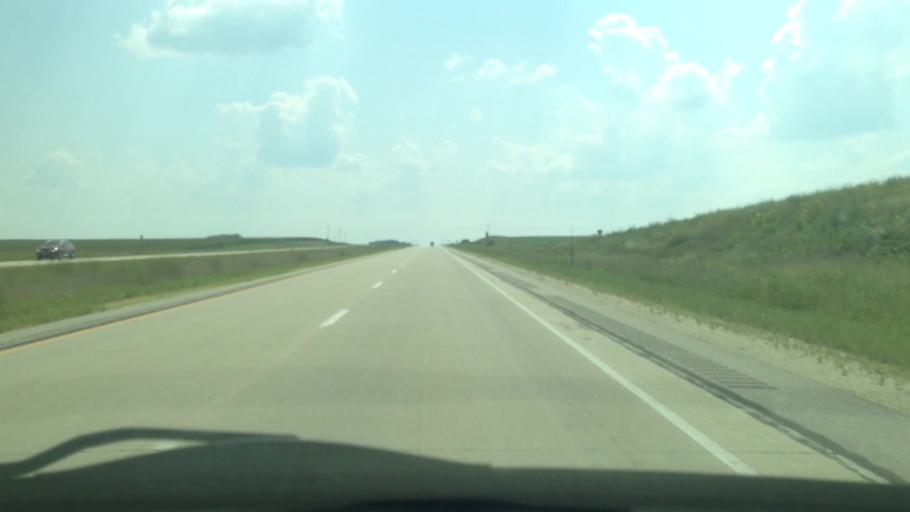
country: US
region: Iowa
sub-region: Bremer County
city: Tripoli
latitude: 42.8930
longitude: -92.3299
